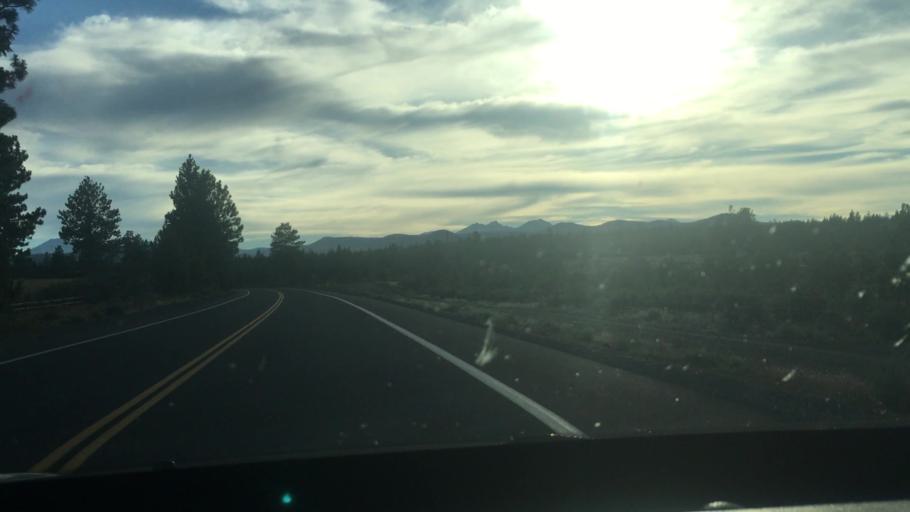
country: US
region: Oregon
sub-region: Deschutes County
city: Bend
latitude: 44.0526
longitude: -121.3724
